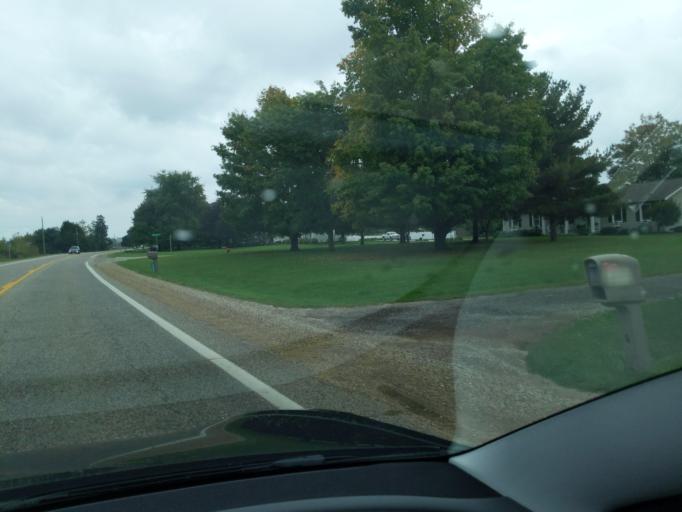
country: US
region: Michigan
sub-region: Eaton County
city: Charlotte
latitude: 42.5528
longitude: -84.7844
